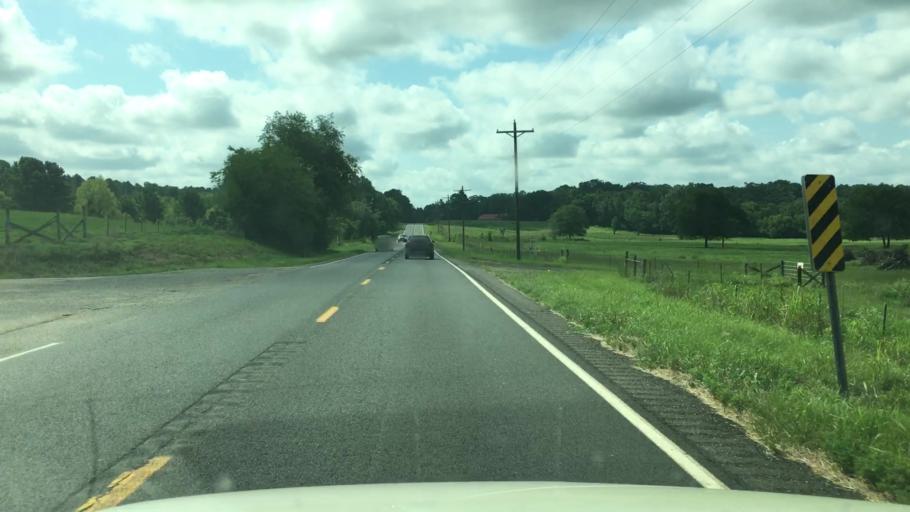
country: US
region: Arkansas
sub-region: Garland County
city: Lake Hamilton
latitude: 34.3359
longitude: -93.1789
